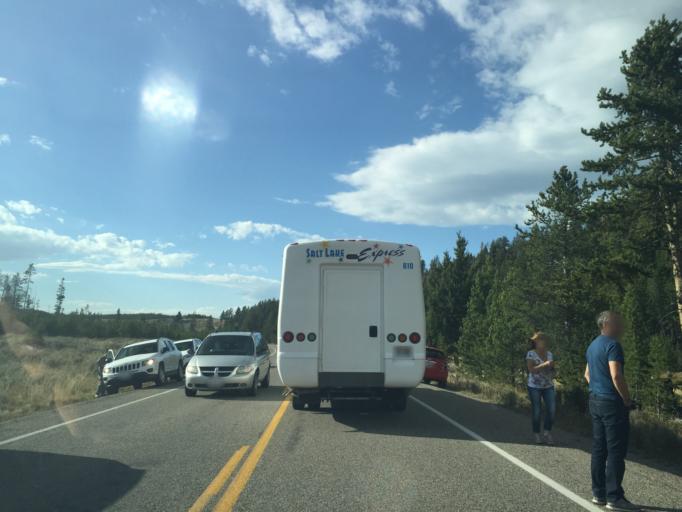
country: US
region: Montana
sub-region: Gallatin County
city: West Yellowstone
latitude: 44.6667
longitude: -110.9703
